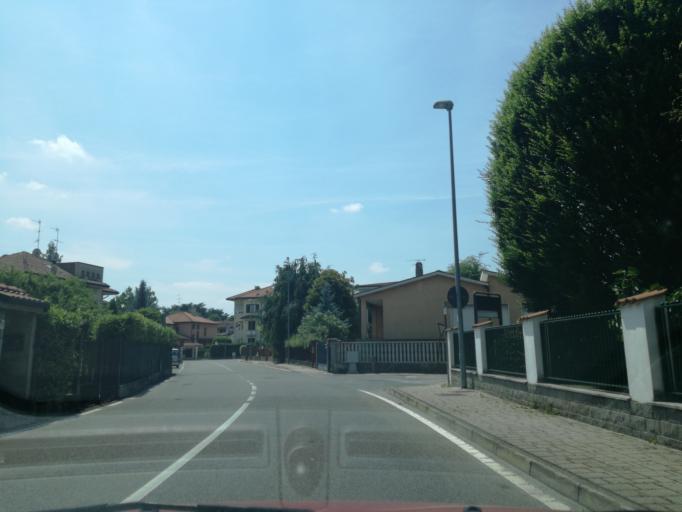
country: IT
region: Lombardy
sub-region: Provincia di Monza e Brianza
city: Biassono
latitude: 45.6299
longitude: 9.2658
